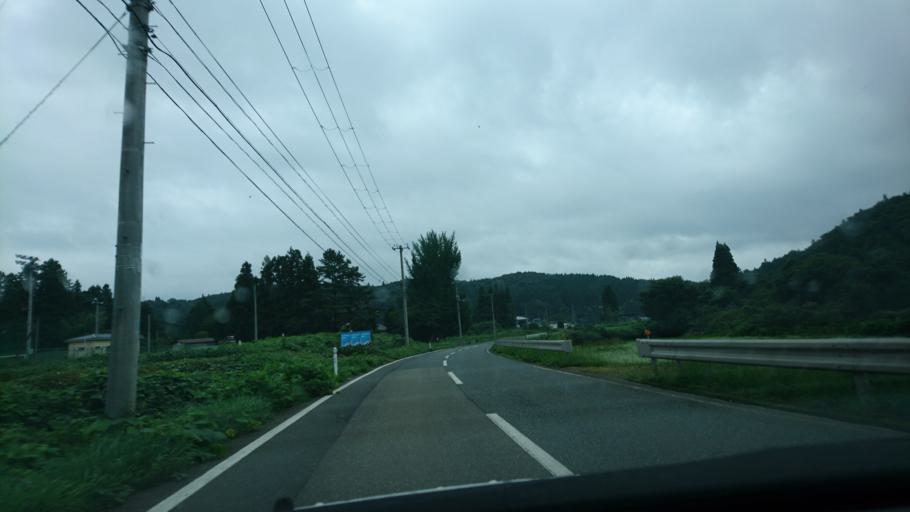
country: JP
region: Iwate
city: Ichinoseki
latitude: 38.9079
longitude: 141.0489
